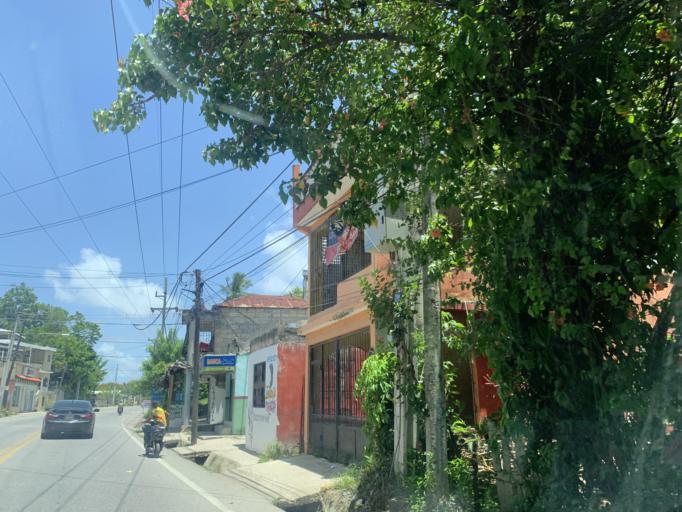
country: DO
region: Puerto Plata
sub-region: Puerto Plata
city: Puerto Plata
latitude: 19.7483
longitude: -70.5949
